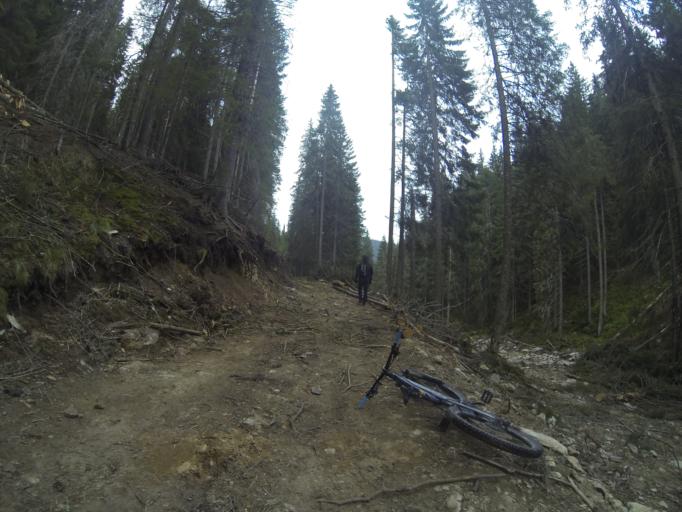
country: RO
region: Gorj
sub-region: Comuna Polovragi
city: Polovragi
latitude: 45.2980
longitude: 23.8409
